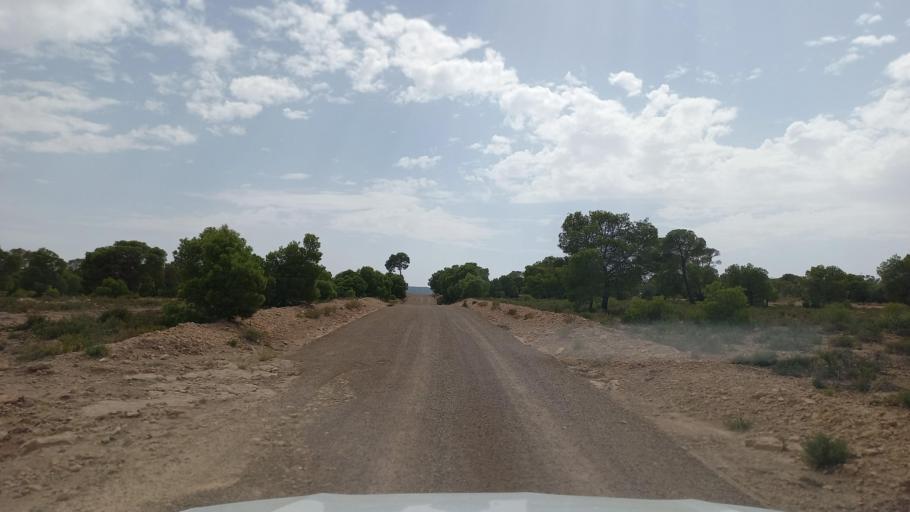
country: TN
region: Al Qasrayn
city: Kasserine
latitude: 35.3812
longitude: 8.8807
